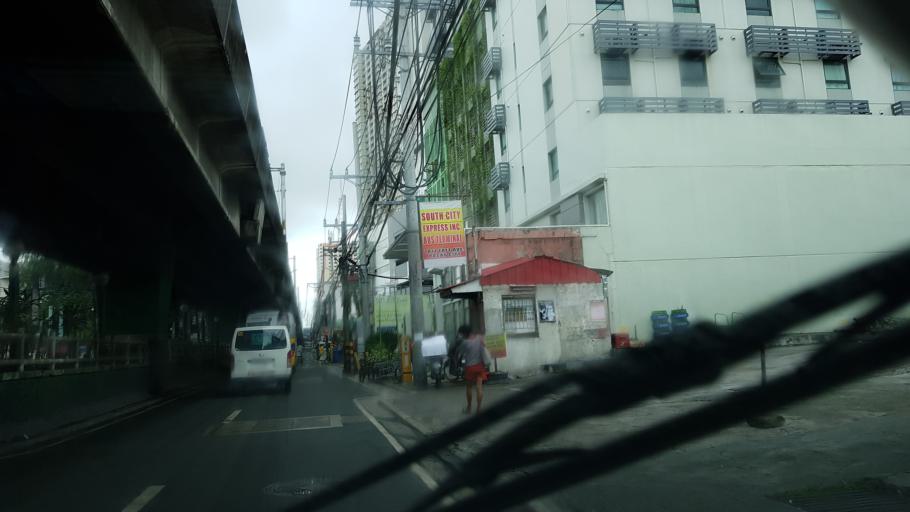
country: PH
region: Metro Manila
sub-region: Makati City
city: Makati City
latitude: 14.5590
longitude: 120.9963
